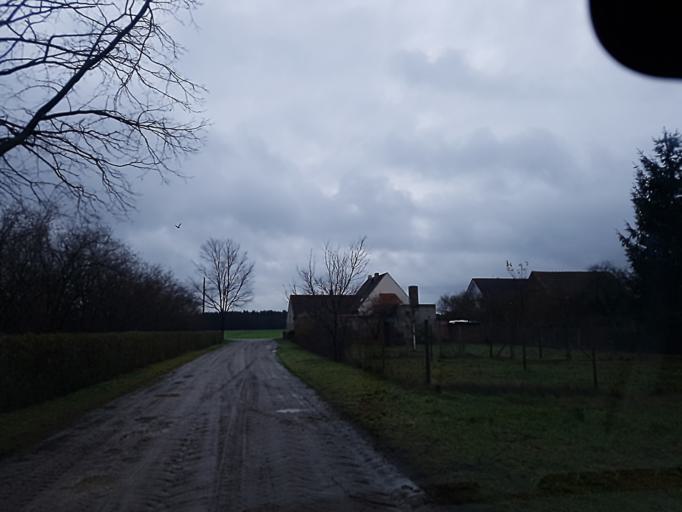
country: DE
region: Brandenburg
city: Finsterwalde
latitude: 51.6031
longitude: 13.6681
